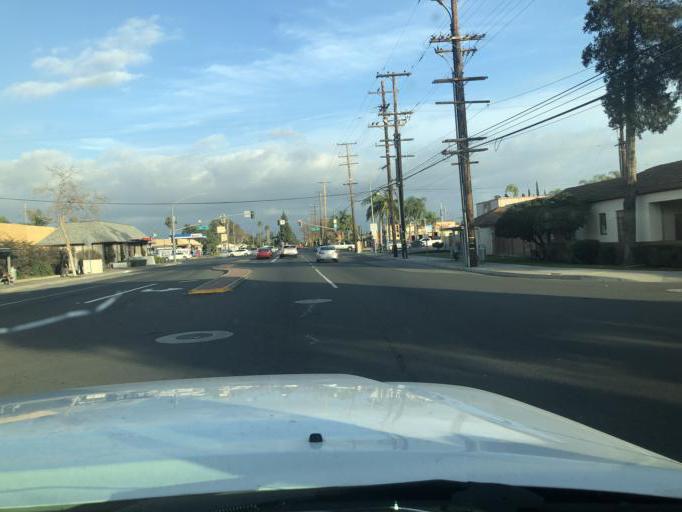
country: US
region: California
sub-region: Orange County
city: Santa Ana
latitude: 33.7272
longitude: -117.8690
